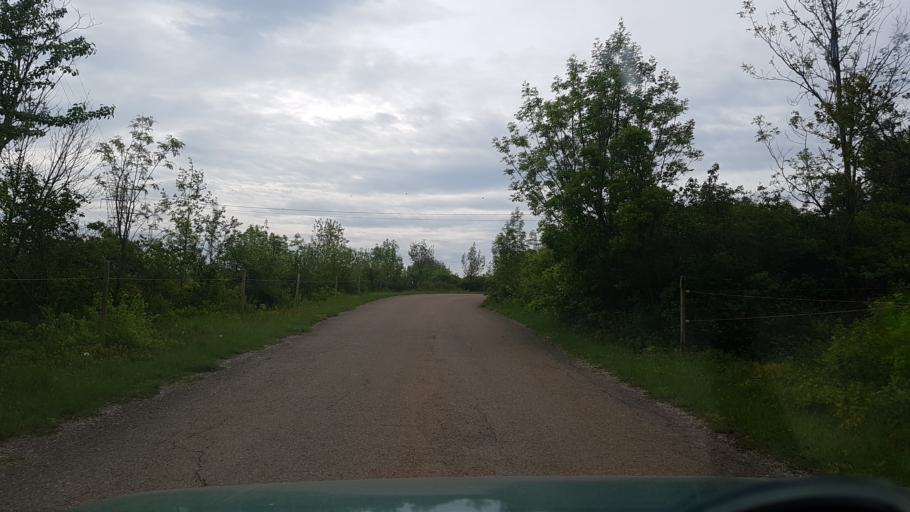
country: IT
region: Friuli Venezia Giulia
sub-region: Provincia di Gorizia
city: Ronchi dei Legionari
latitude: 45.8479
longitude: 13.5030
